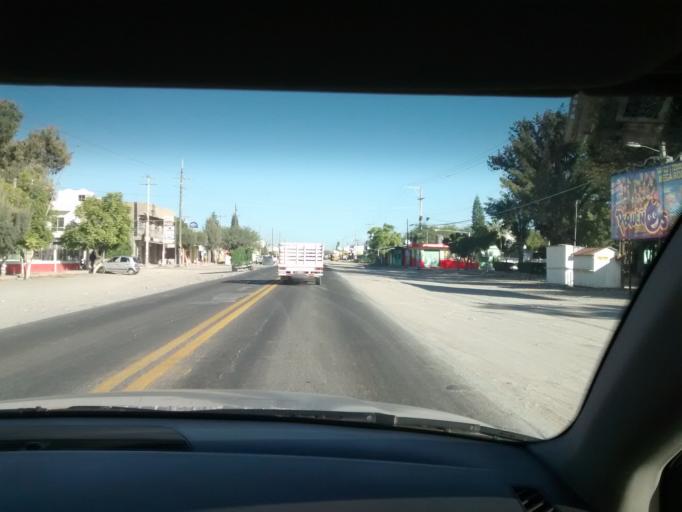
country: MX
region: Puebla
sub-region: Santiago Miahuatlan
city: San Jose Monte Chiquito
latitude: 18.4922
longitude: -97.4640
